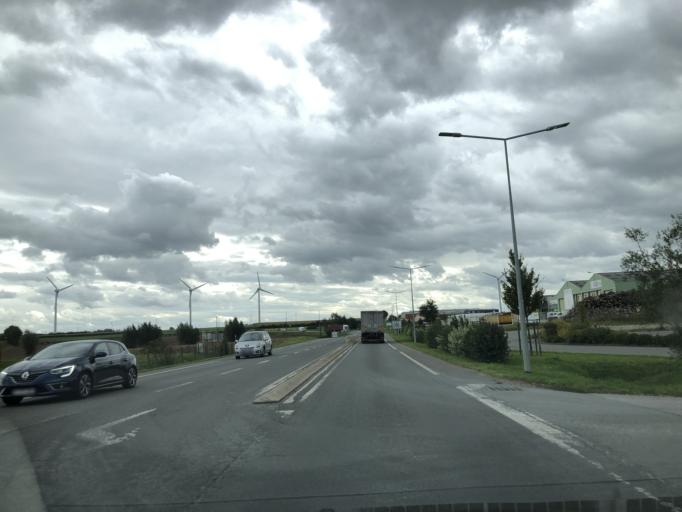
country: FR
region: Nord-Pas-de-Calais
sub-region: Departement du Pas-de-Calais
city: Fruges
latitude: 50.5031
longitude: 2.1305
